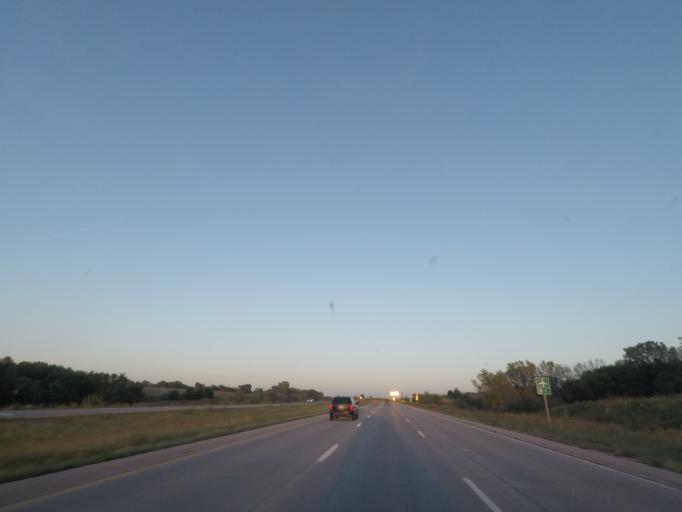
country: US
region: Iowa
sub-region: Polk County
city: West Des Moines
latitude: 41.5221
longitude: -93.7341
